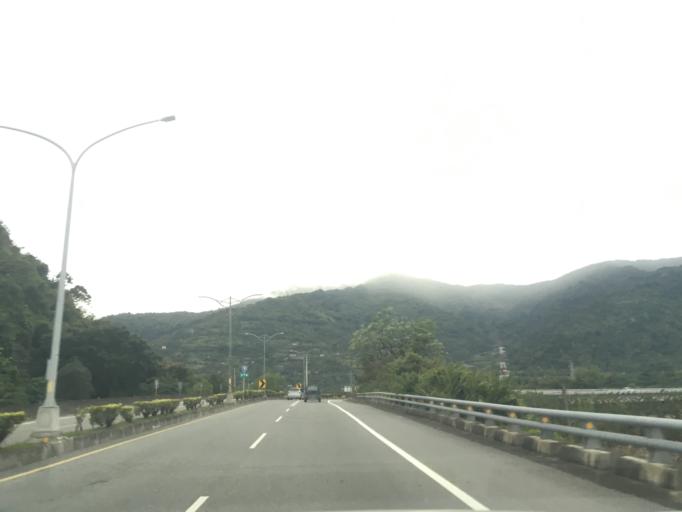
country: TW
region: Taiwan
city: Taitung City
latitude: 22.6995
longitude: 121.0407
